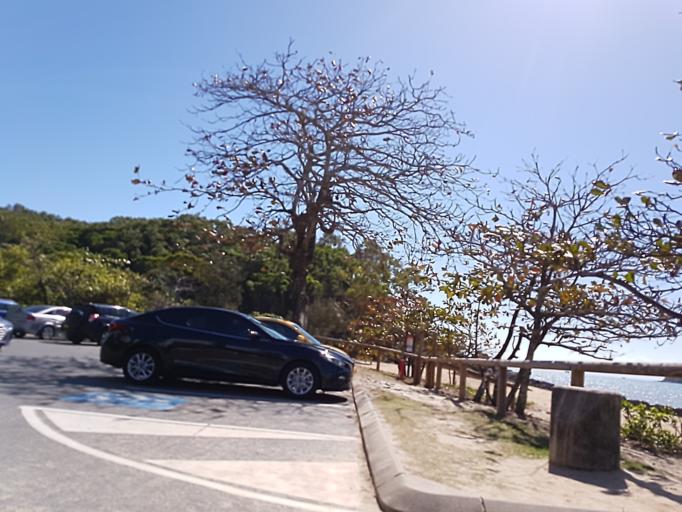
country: AU
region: Queensland
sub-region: Cairns
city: Palm Cove
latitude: -16.7399
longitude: 145.6717
